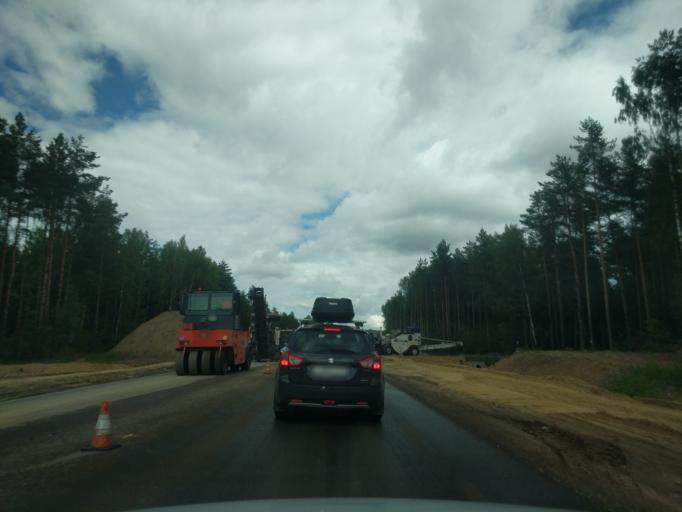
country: RU
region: Jaroslavl
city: Levashevo
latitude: 57.6815
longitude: 40.5969
